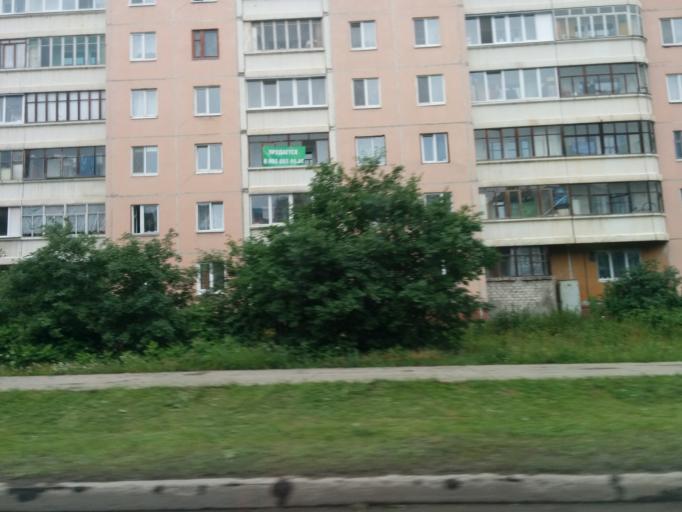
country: RU
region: Perm
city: Kondratovo
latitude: 57.9948
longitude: 56.1361
